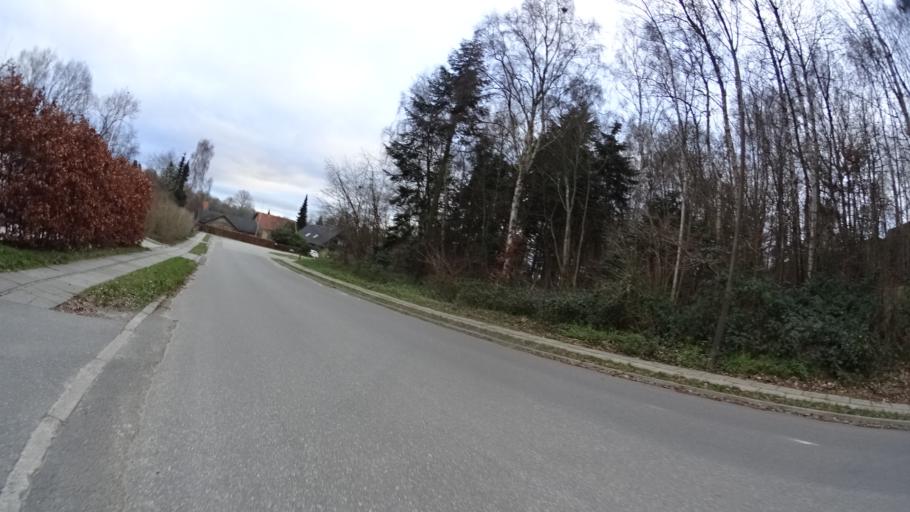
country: DK
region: Central Jutland
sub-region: Arhus Kommune
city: Stavtrup
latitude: 56.1596
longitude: 10.1196
